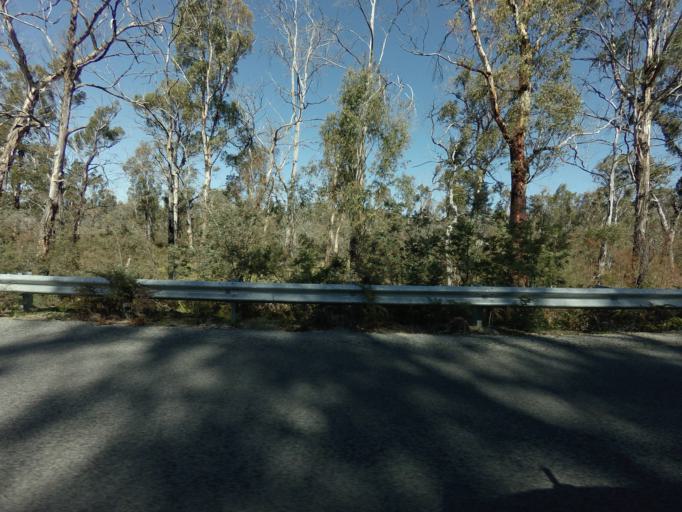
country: AU
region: Tasmania
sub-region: Derwent Valley
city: New Norfolk
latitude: -42.5453
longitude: 146.7161
